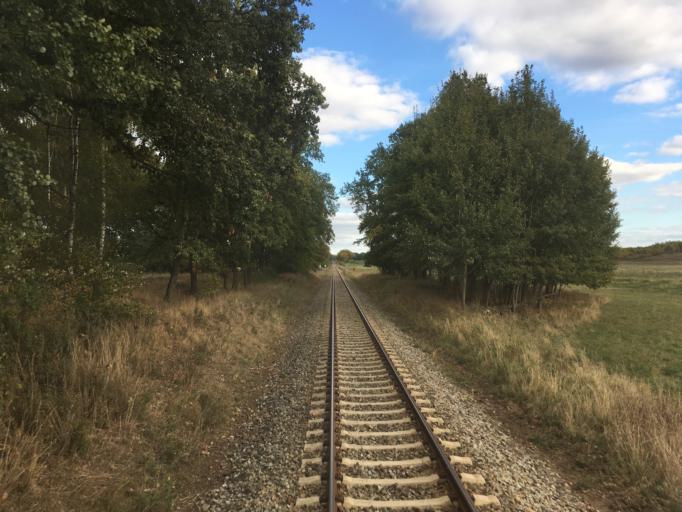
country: DE
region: Mecklenburg-Vorpommern
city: Grabowhofe
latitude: 53.5416
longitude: 12.5891
